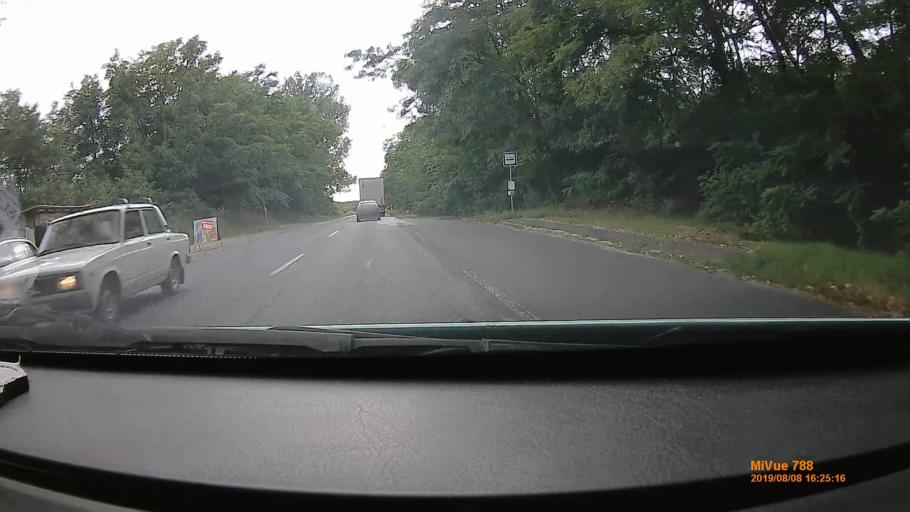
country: HU
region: Szabolcs-Szatmar-Bereg
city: Hodasz
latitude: 47.9690
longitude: 22.2166
